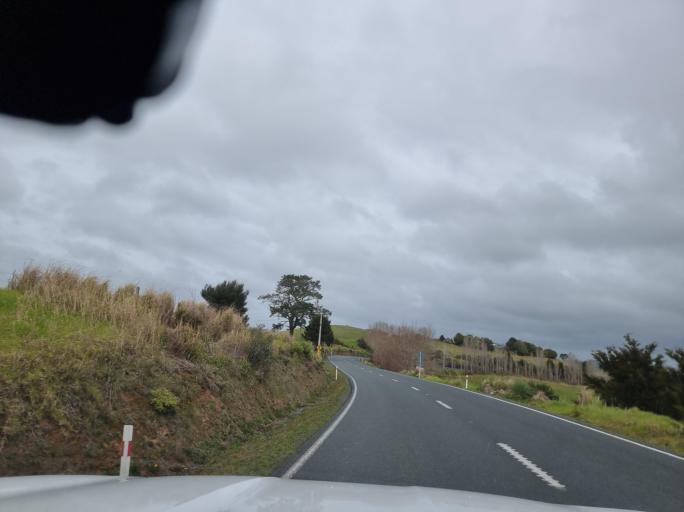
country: NZ
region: Auckland
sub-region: Auckland
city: Wellsford
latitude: -36.1340
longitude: 174.5274
